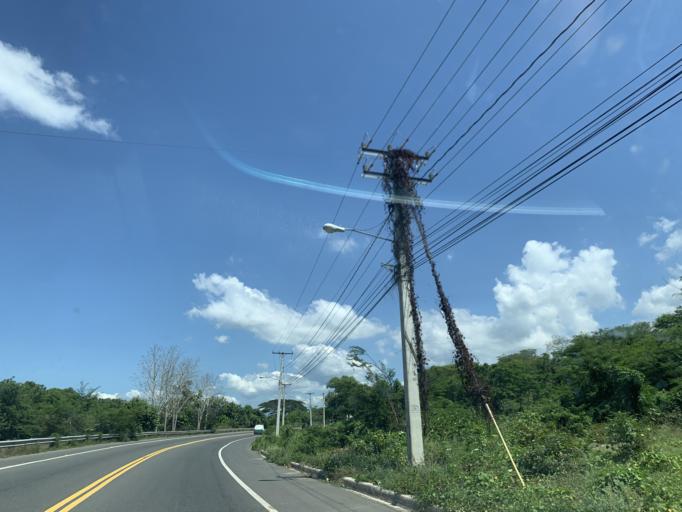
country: DO
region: Puerto Plata
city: Imbert
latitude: 19.7328
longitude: -70.8312
